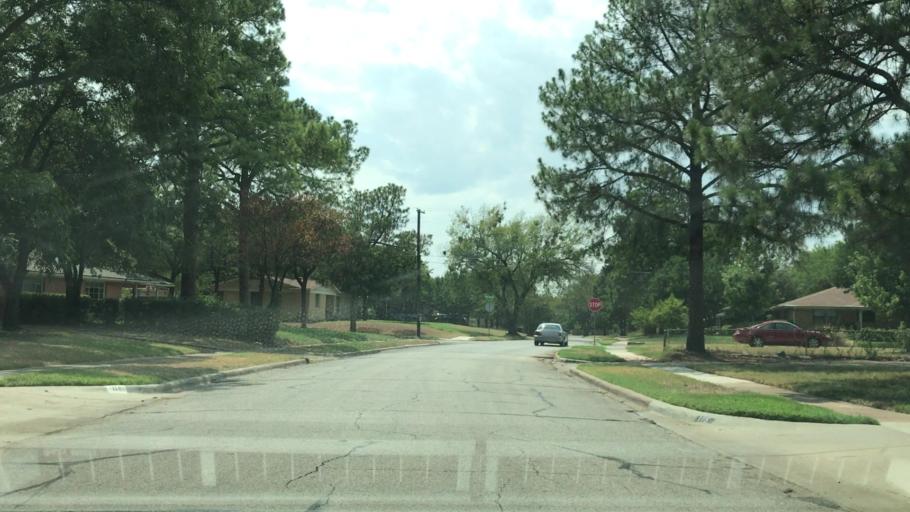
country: US
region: Texas
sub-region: Dallas County
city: Irving
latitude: 32.8406
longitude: -96.9437
